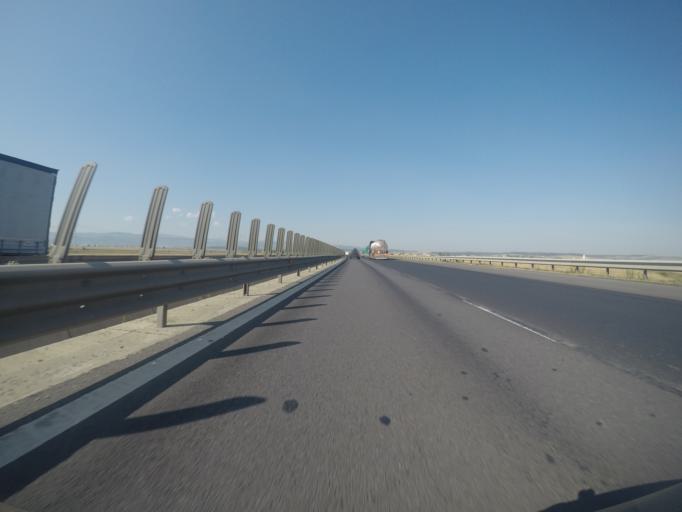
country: RO
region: Sibiu
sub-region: Comuna Sura Mica
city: Sura Mica
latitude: 45.8257
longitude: 24.0891
